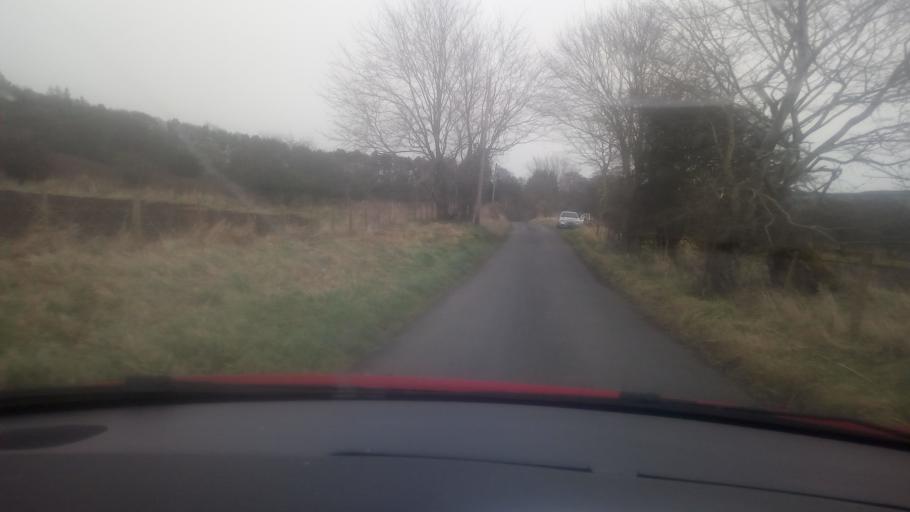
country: GB
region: Scotland
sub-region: The Scottish Borders
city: Saint Boswells
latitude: 55.4971
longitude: -2.6285
